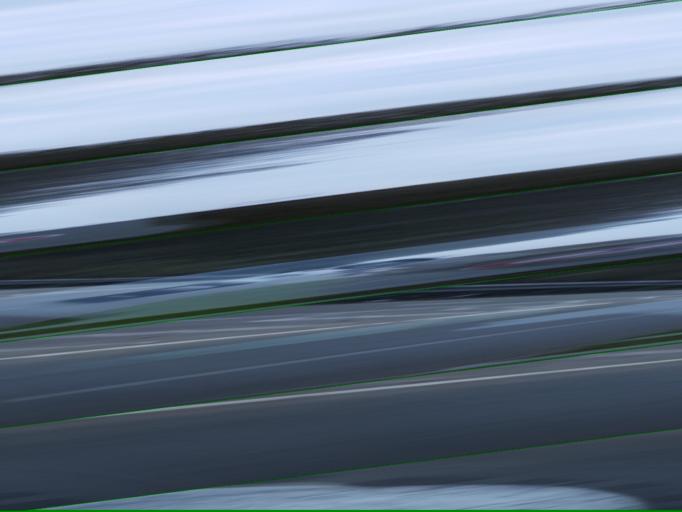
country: FR
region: Ile-de-France
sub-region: Departement des Yvelines
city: Houdan
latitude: 48.7832
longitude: 1.5742
